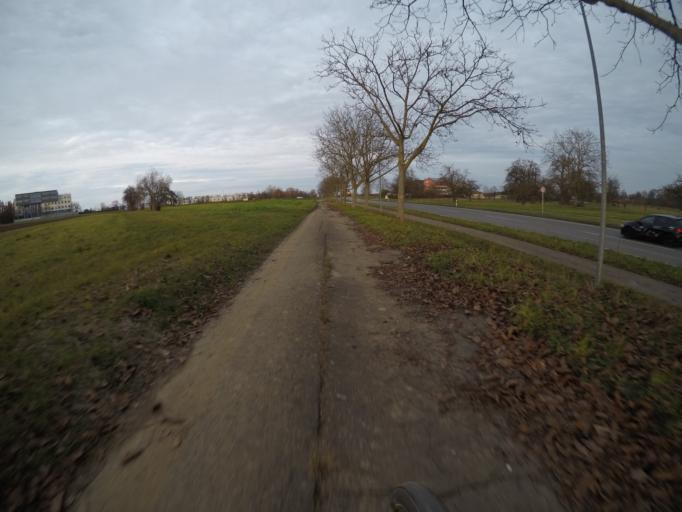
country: DE
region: Baden-Wuerttemberg
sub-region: Regierungsbezirk Stuttgart
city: Ostfildern
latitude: 48.7122
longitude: 9.2736
